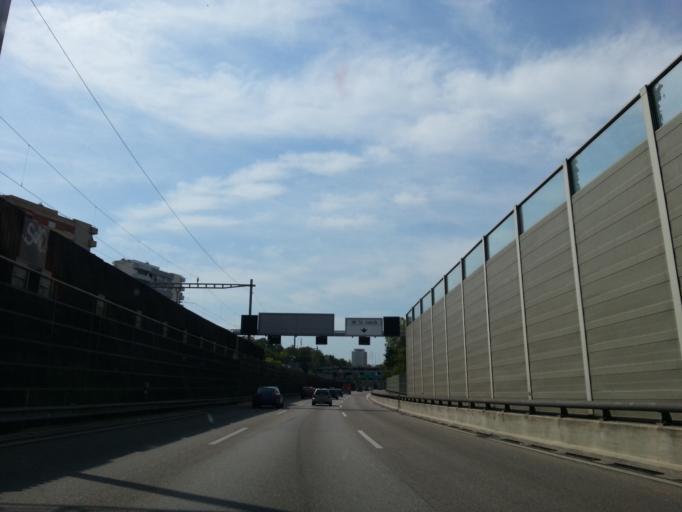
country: CH
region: Basel-Landschaft
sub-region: Bezirk Arlesheim
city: Birsfelden
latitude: 47.5531
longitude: 7.6162
